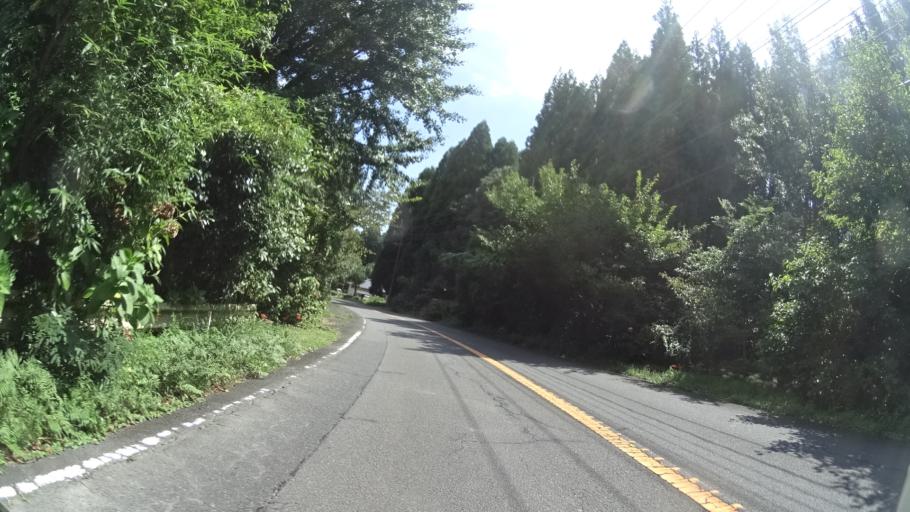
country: JP
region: Kagoshima
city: Kokubu-matsuki
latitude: 31.8640
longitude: 130.7866
